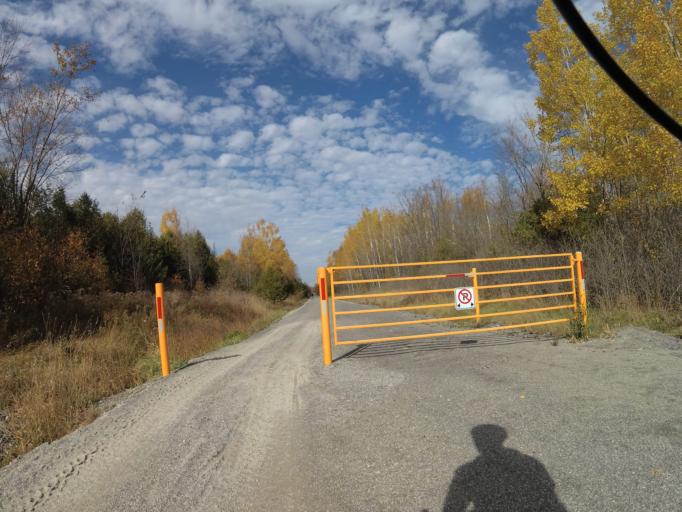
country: CA
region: Ontario
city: Carleton Place
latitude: 45.0773
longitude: -76.1032
